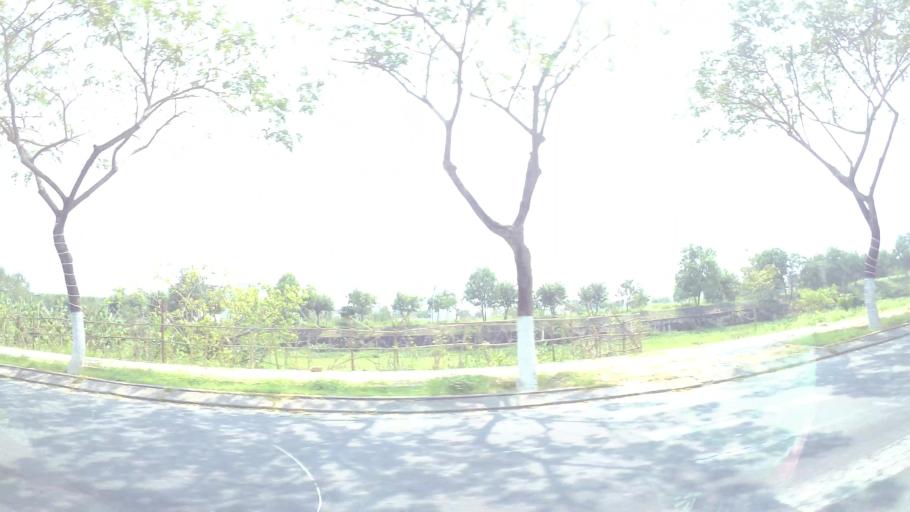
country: VN
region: Da Nang
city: Cam Le
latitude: 16.0166
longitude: 108.2108
